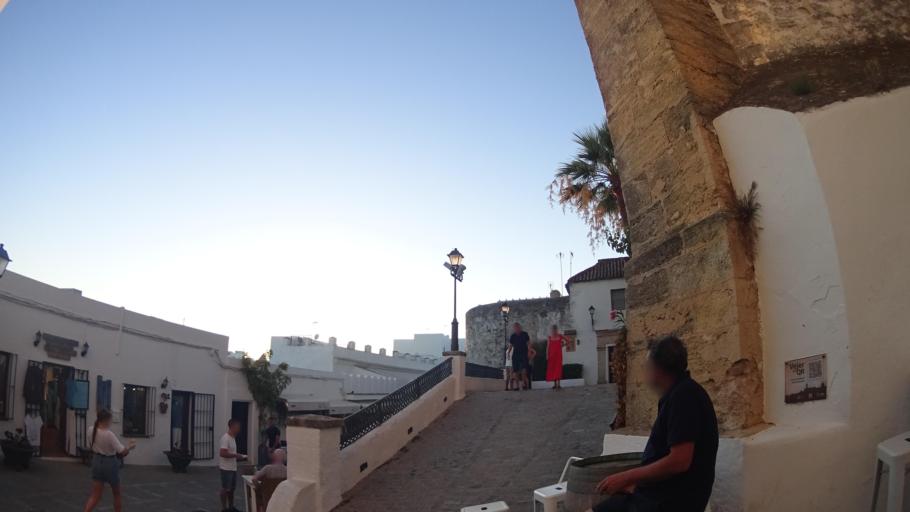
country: ES
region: Andalusia
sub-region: Provincia de Cadiz
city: Vejer de la Frontera
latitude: 36.2538
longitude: -5.9646
